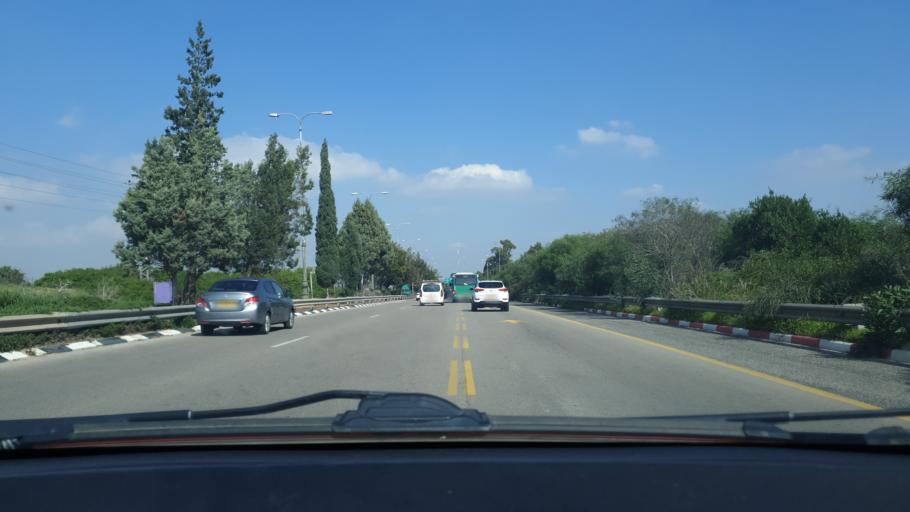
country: IL
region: Central District
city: Bet Dagan
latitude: 31.9951
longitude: 34.8159
